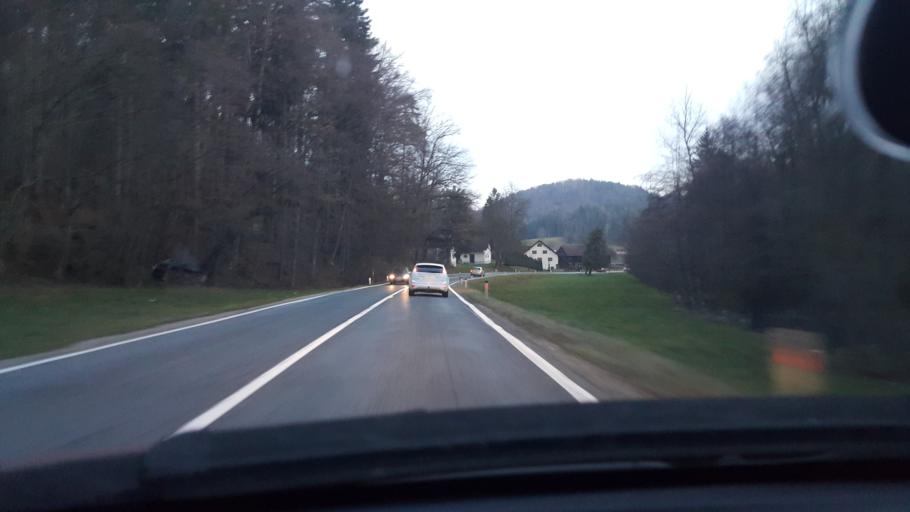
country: SI
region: Dobrna
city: Dobrna
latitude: 46.3277
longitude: 15.1805
